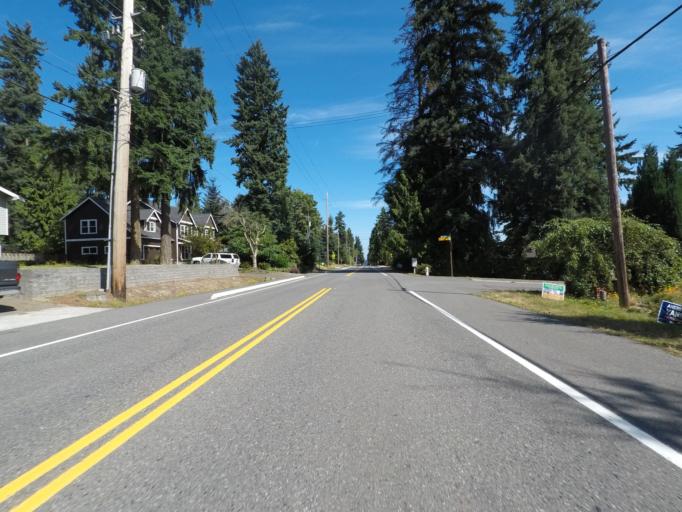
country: US
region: Washington
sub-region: King County
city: Inglewood-Finn Hill
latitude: 47.7372
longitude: -122.2290
